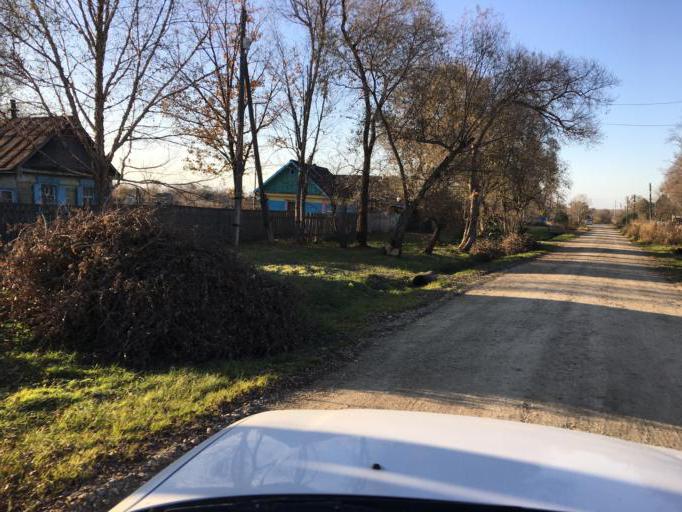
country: RU
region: Primorskiy
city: Lazo
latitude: 45.8663
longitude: 133.6409
